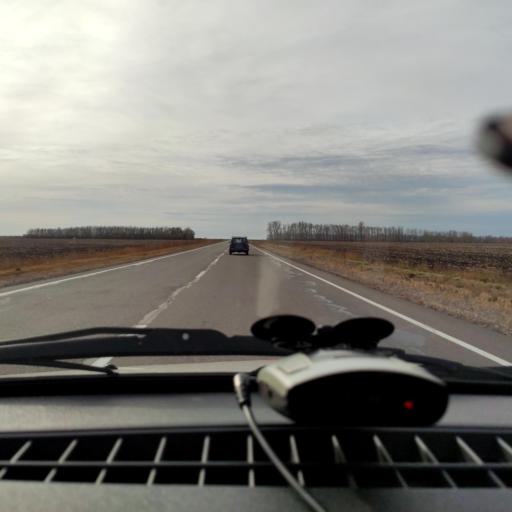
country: RU
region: Voronezj
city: Strelitsa
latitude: 51.4855
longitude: 38.9626
